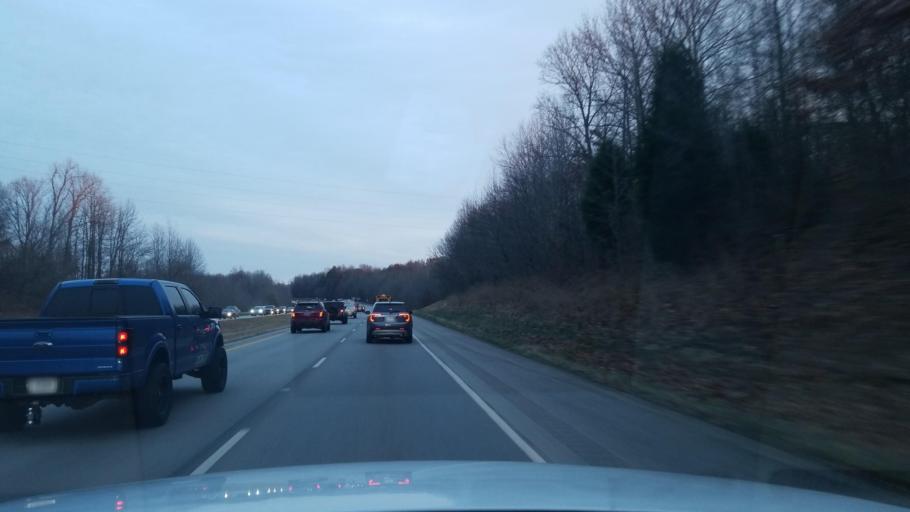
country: US
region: Indiana
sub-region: Vanderburgh County
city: Evansville
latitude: 37.9483
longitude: -87.7041
